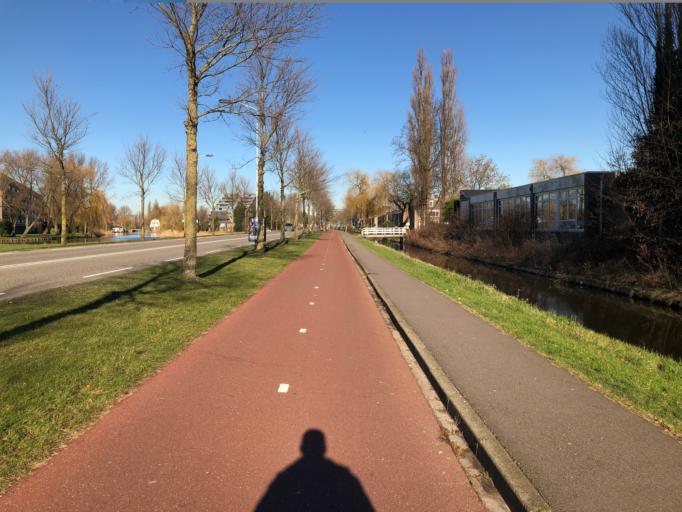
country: NL
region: North Holland
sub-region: Gemeente Uitgeest
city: Uitgeest
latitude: 52.4997
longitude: 4.7564
